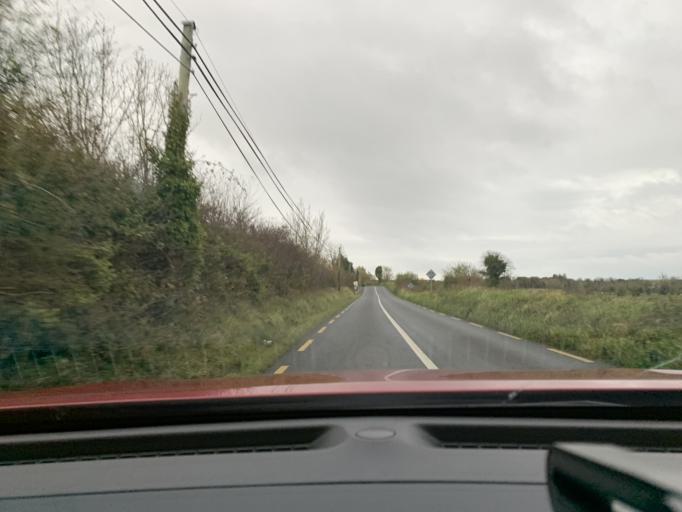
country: IE
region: Connaught
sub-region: Sligo
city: Ballymote
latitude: 54.0658
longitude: -8.5084
